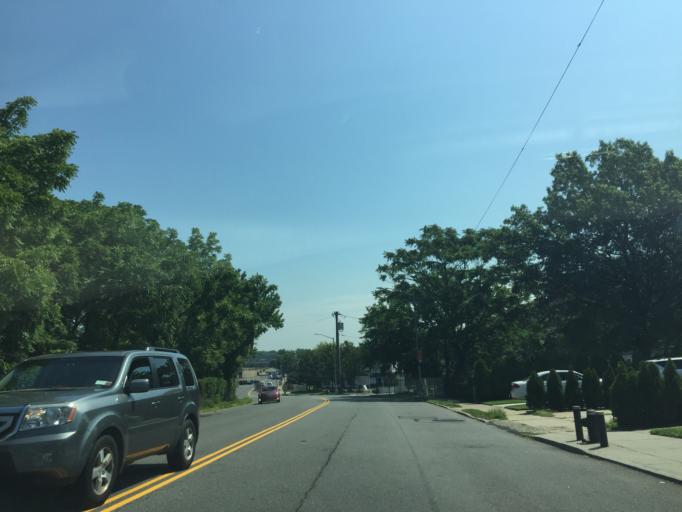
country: US
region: New York
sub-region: Nassau County
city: East Atlantic Beach
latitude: 40.7861
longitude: -73.7941
